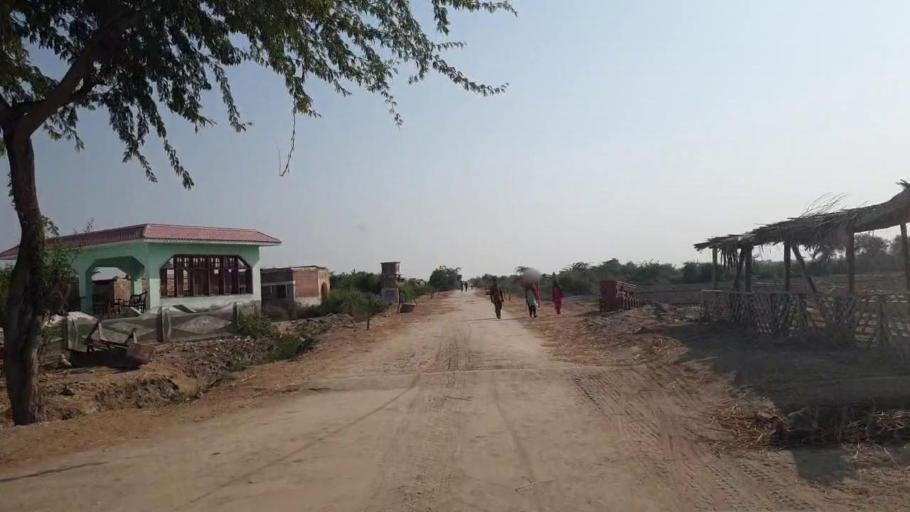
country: PK
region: Sindh
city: Matli
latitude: 24.9690
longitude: 68.6458
